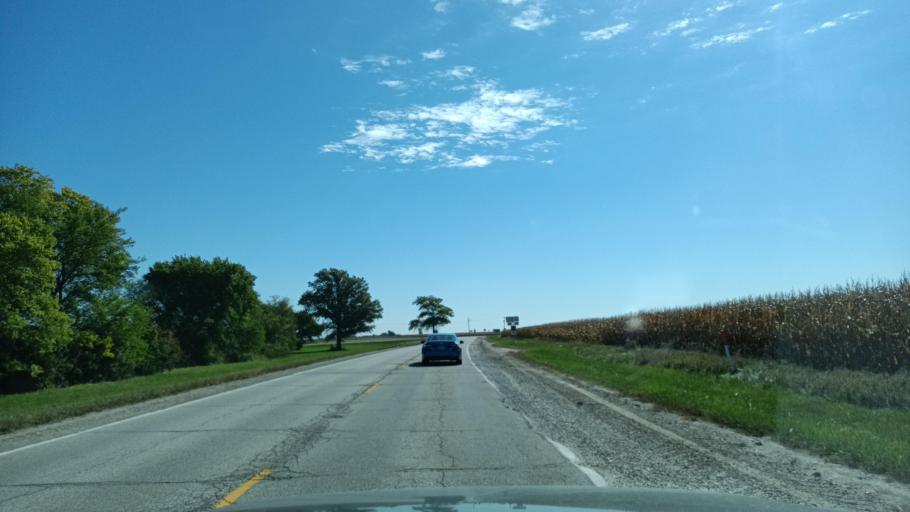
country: US
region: Illinois
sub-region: Knox County
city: Knoxville
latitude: 40.9072
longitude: -90.2540
